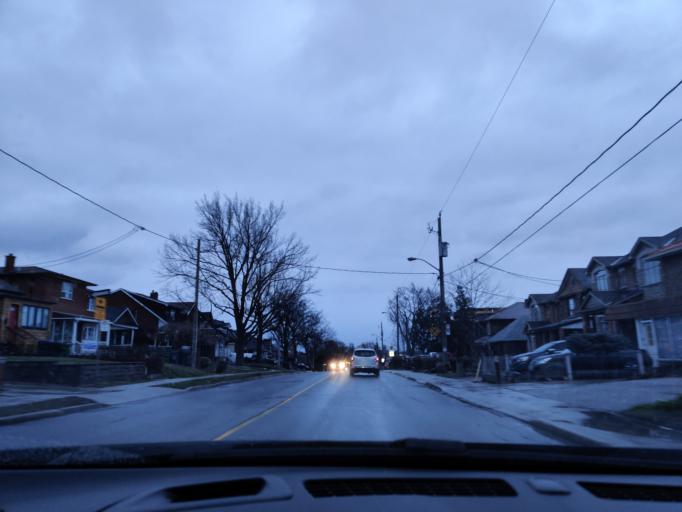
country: CA
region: Ontario
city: Toronto
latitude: 43.6866
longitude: -79.4595
